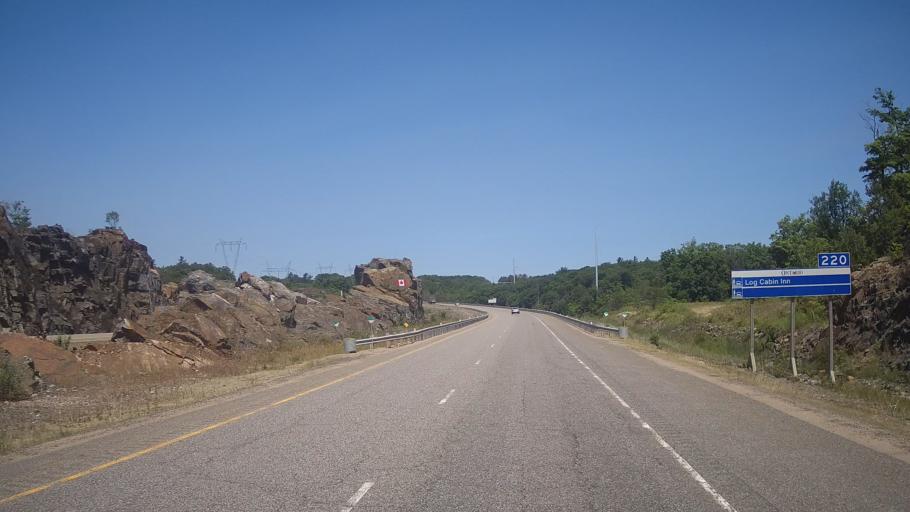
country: CA
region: Ontario
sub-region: Parry Sound District
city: Parry Sound
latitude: 45.3168
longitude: -79.9426
